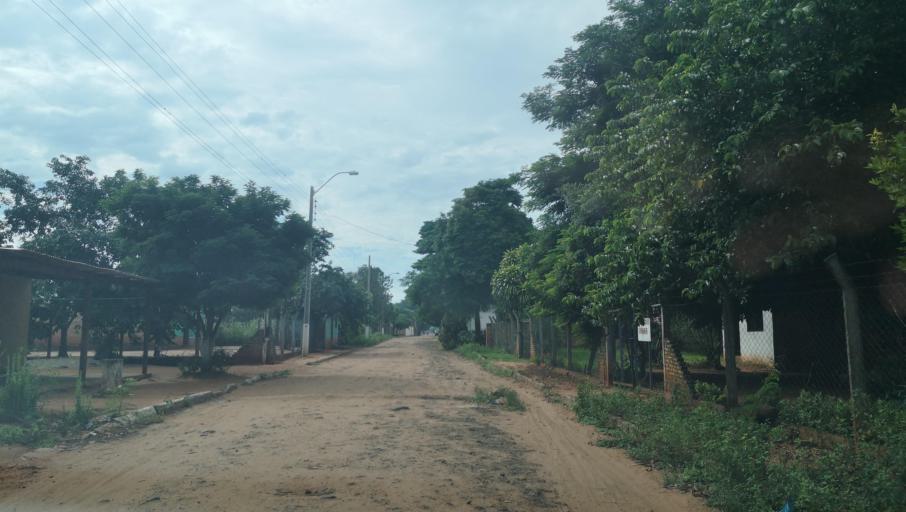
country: PY
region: San Pedro
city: Capiibary
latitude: -24.7274
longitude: -56.0221
